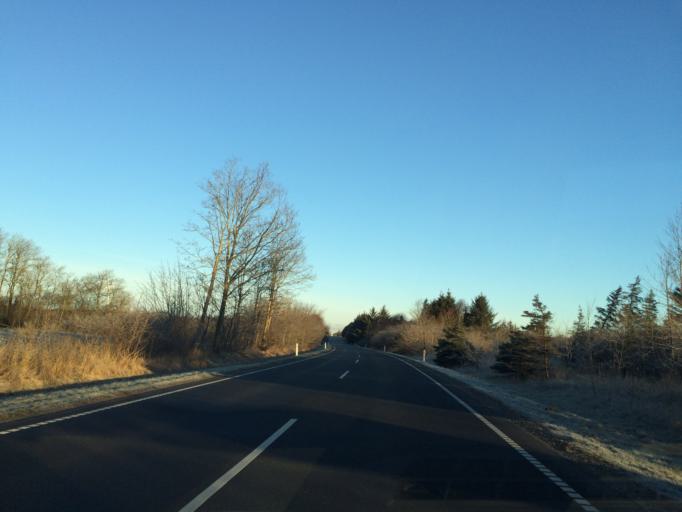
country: DK
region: Central Jutland
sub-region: Holstebro Kommune
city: Ulfborg
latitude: 56.3660
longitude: 8.3351
